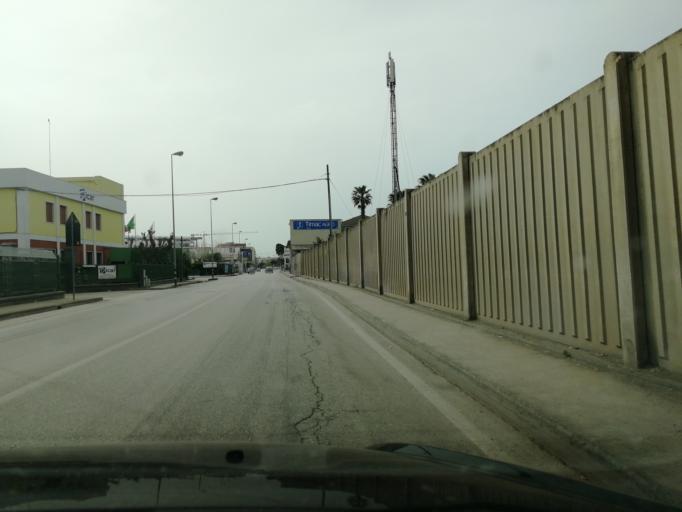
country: IT
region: Apulia
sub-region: Provincia di Barletta - Andria - Trani
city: Barletta
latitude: 41.3167
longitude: 16.2966
